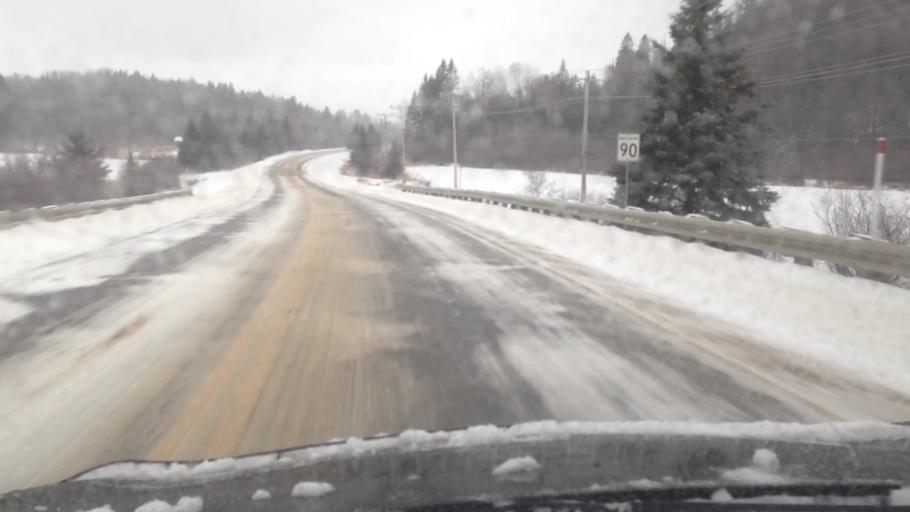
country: CA
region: Quebec
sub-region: Laurentides
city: Mont-Tremblant
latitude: 46.0516
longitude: -74.6114
